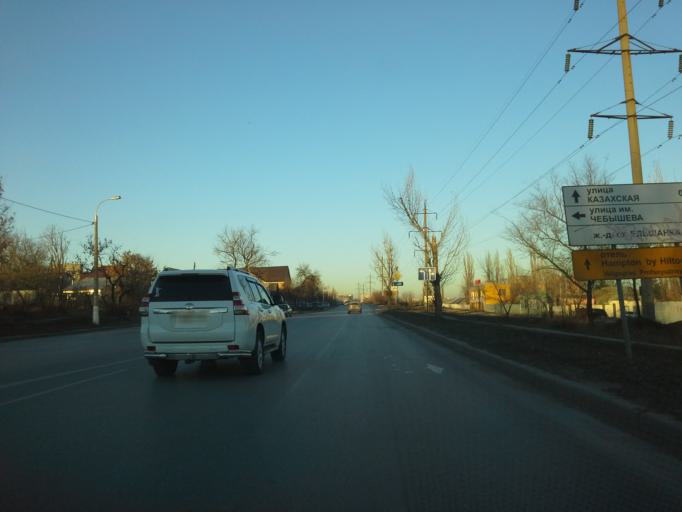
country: RU
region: Volgograd
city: Volgograd
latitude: 48.6684
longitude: 44.4565
